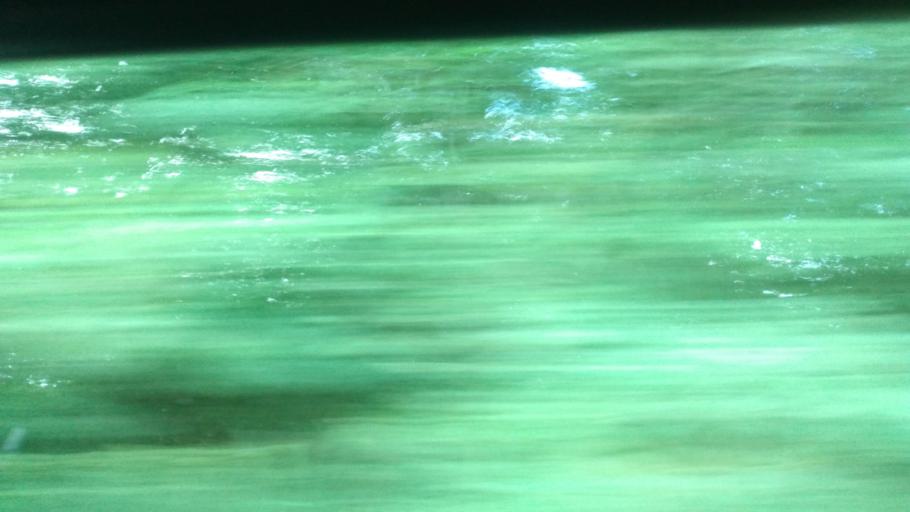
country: BR
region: Pernambuco
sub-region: Quipapa
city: Quipapa
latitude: -8.7802
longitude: -35.9483
